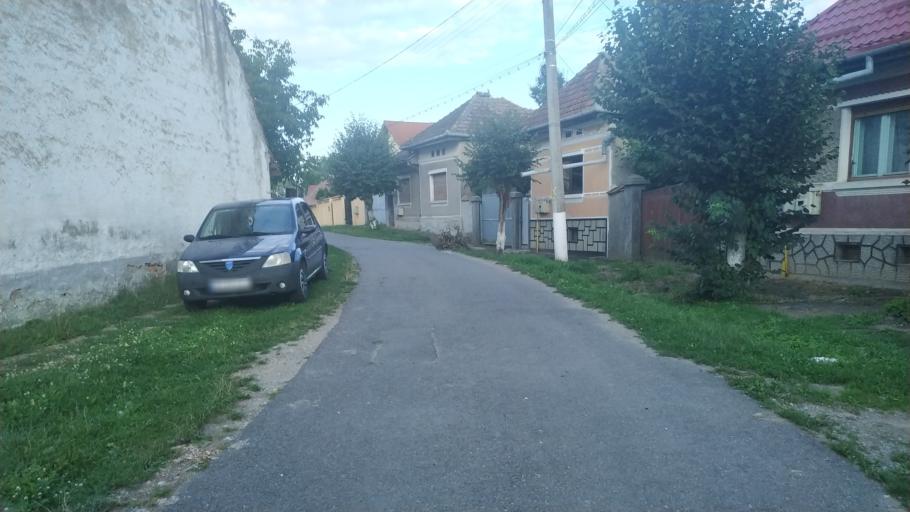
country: RO
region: Brasov
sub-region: Comuna Beclean
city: Beclean
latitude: 45.8297
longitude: 24.9214
